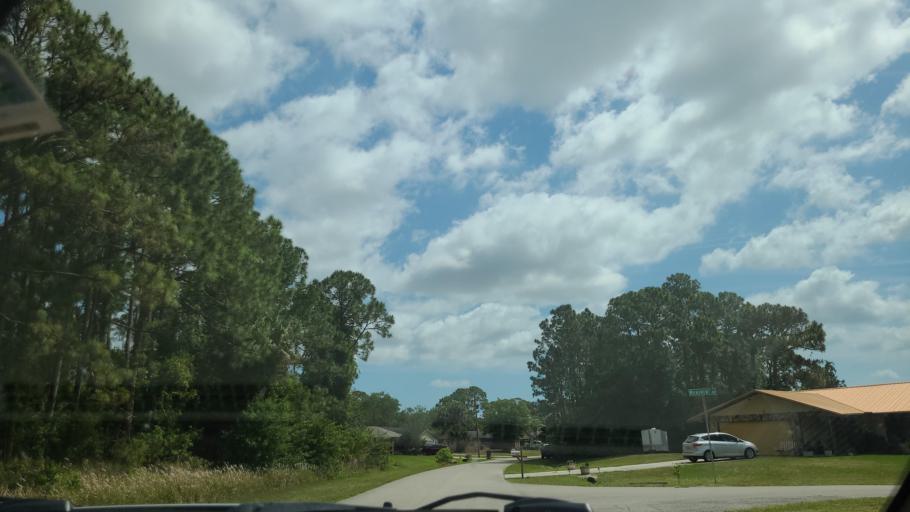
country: US
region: Florida
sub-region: Brevard County
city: Grant-Valkaria
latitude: 27.9686
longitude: -80.6669
